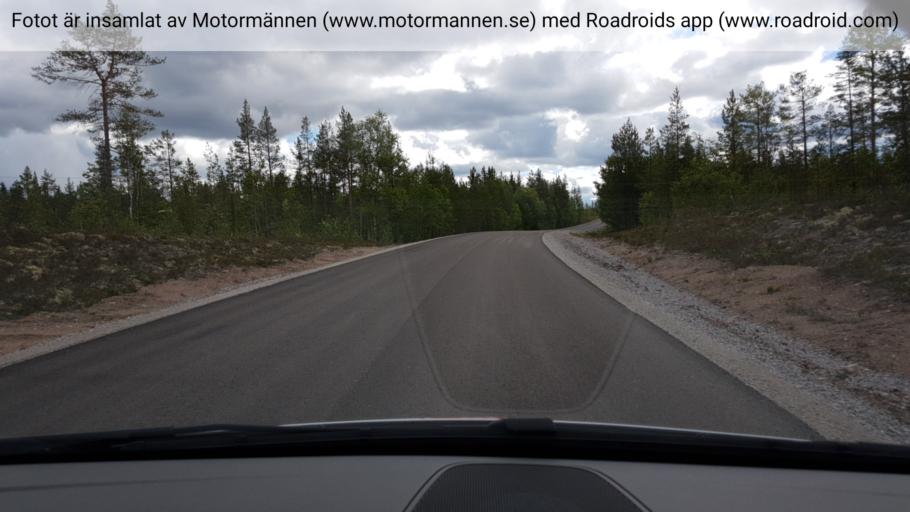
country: SE
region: Jaemtland
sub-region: Harjedalens Kommun
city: Sveg
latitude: 61.6971
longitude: 14.1876
